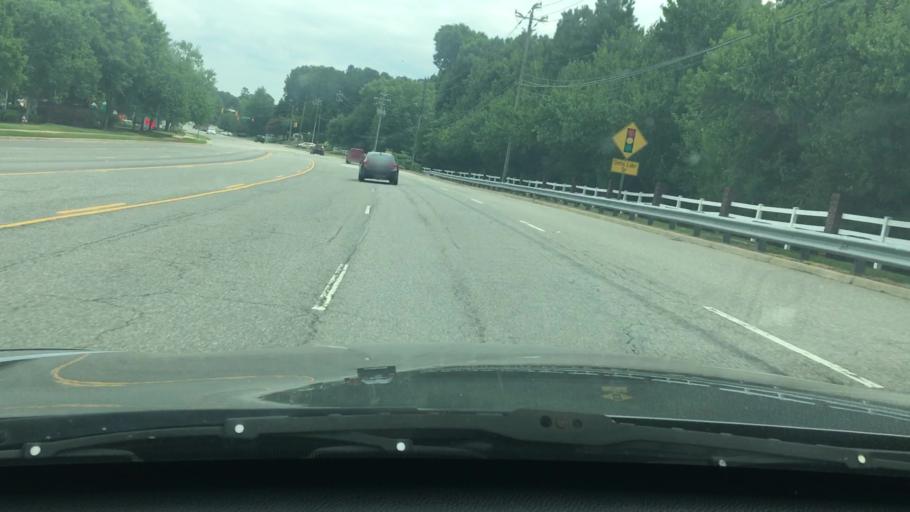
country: US
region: North Carolina
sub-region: Wake County
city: West Raleigh
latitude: 35.8586
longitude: -78.7130
